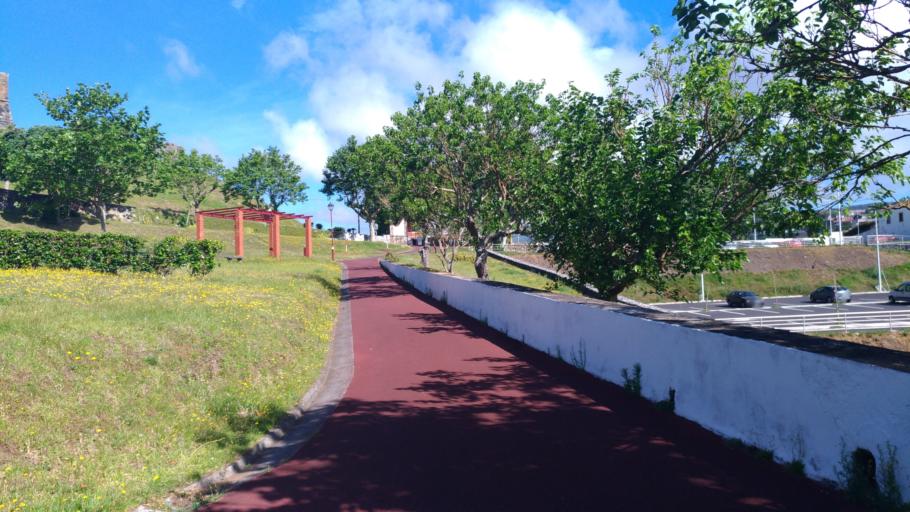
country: PT
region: Azores
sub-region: Angra do Heroismo
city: Angra do Heroismo
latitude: 38.6520
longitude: -27.2234
